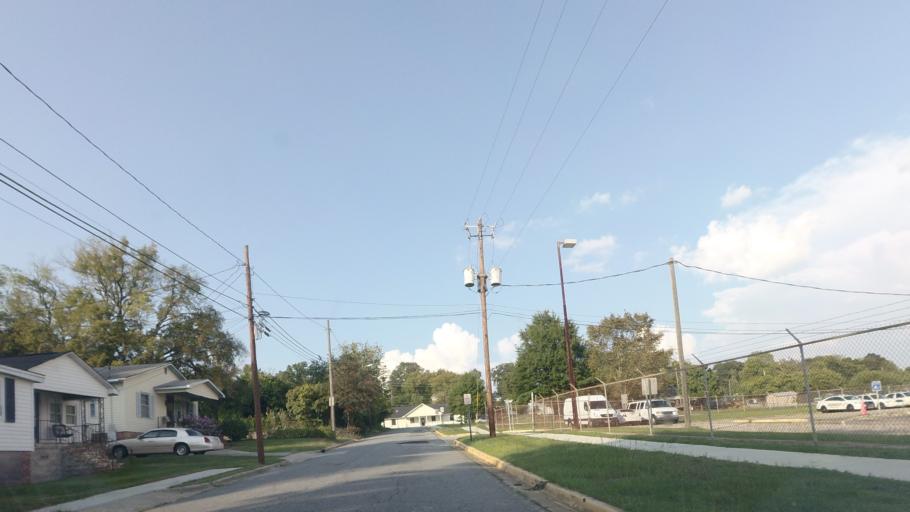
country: US
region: Georgia
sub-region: Bibb County
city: Macon
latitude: 32.8300
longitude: -83.6406
